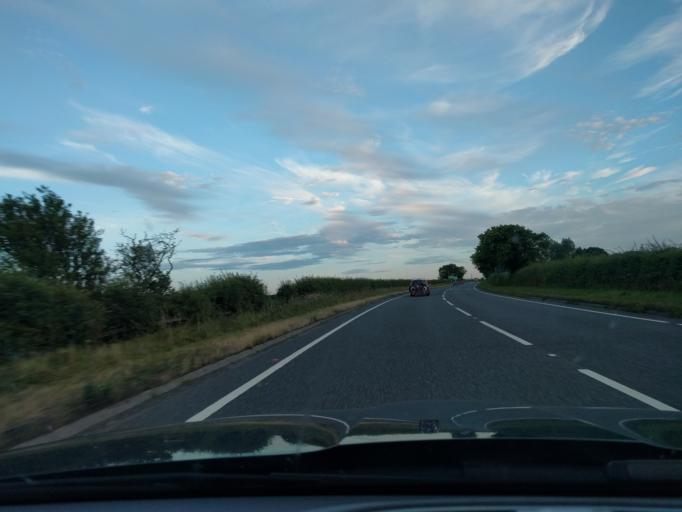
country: GB
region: England
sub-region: Northumberland
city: Felton
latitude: 55.2554
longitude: -1.7024
